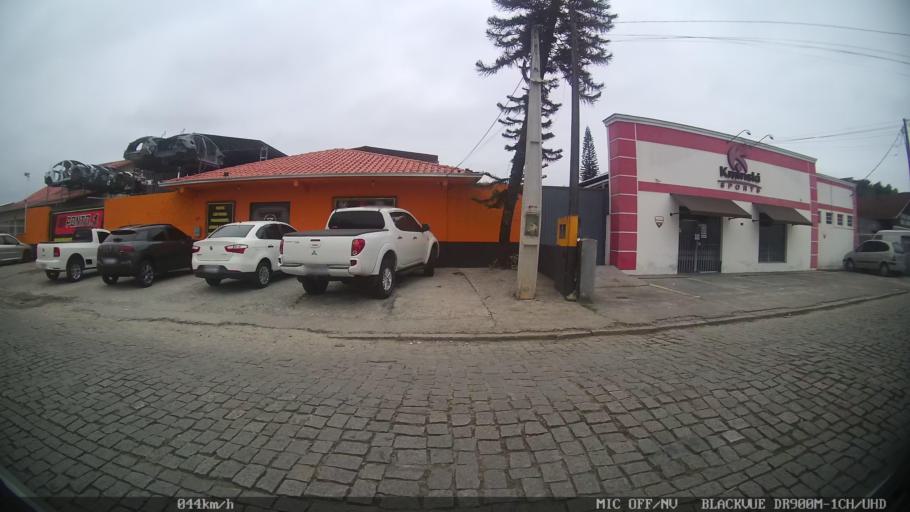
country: BR
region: Santa Catarina
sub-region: Joinville
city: Joinville
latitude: -26.3430
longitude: -48.8495
